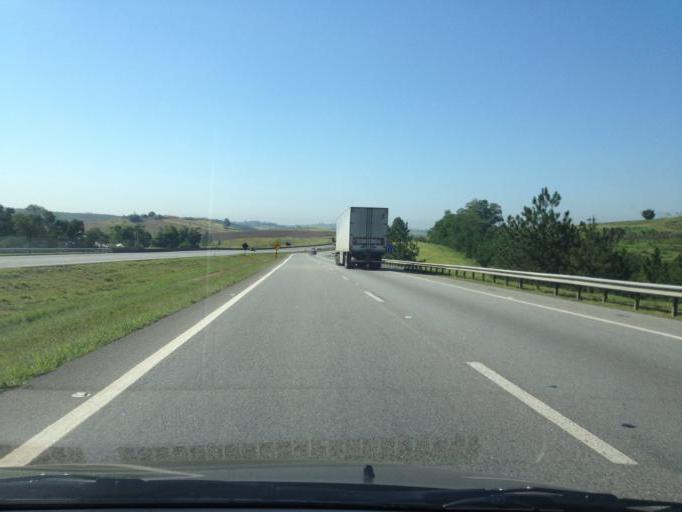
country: BR
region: Sao Paulo
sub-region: Guararema
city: Guararema
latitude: -23.3596
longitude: -46.0958
